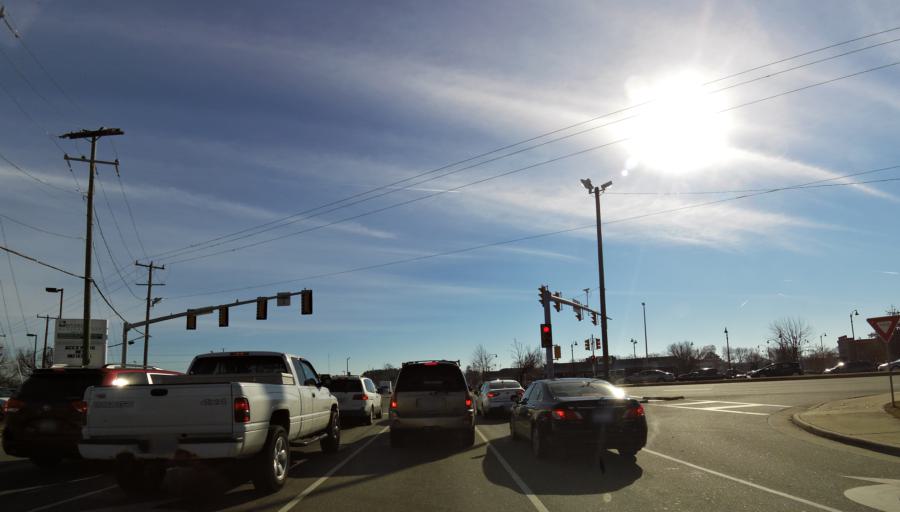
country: US
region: Virginia
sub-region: City of Hampton
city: Hampton
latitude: 37.0392
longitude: -76.4022
